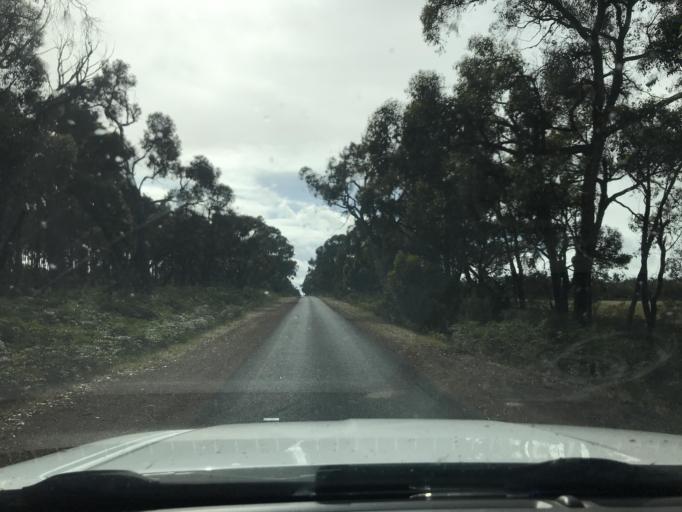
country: AU
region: South Australia
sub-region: Wattle Range
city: Penola
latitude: -37.1880
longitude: 141.2335
